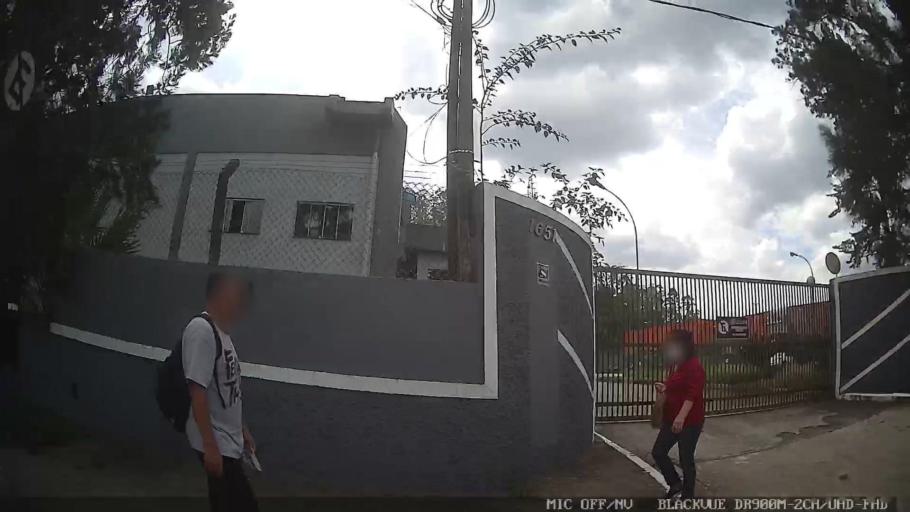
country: BR
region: Sao Paulo
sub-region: Ribeirao Pires
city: Ribeirao Pires
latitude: -23.7059
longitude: -46.3981
